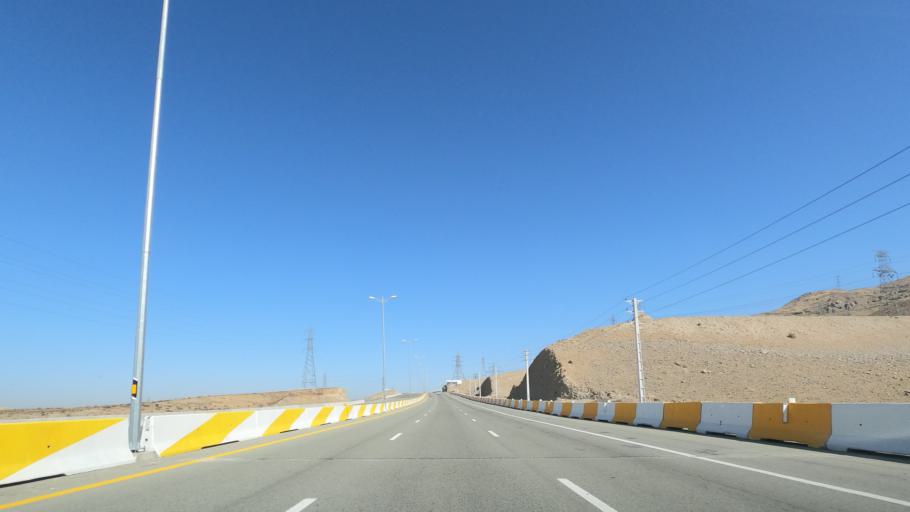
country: IR
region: Tehran
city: Shahr-e Qods
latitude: 35.7718
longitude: 51.0583
